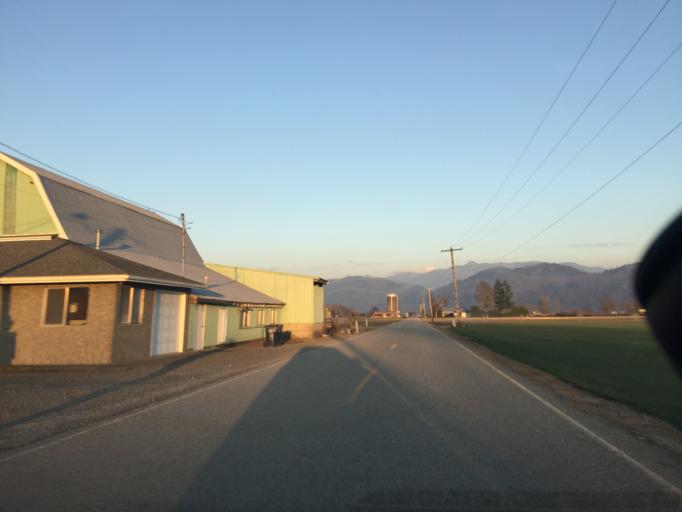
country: US
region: Washington
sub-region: Whatcom County
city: Sumas
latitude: 49.0001
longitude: -122.2453
